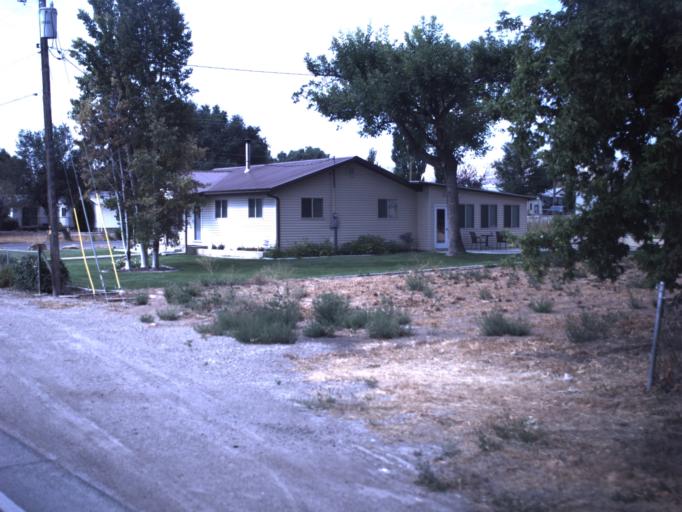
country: US
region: Utah
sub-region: Uintah County
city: Naples
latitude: 40.4054
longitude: -109.4990
